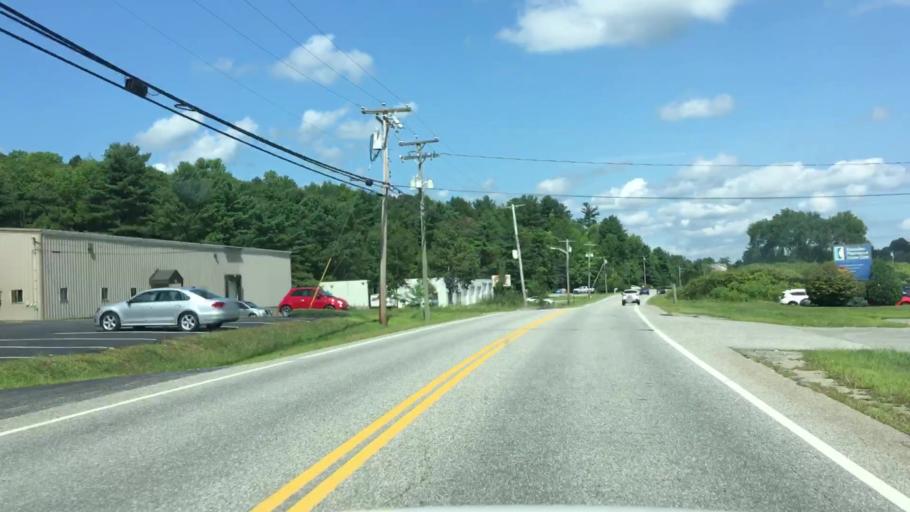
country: US
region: Maine
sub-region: Kennebec County
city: Augusta
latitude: 44.3220
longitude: -69.8164
